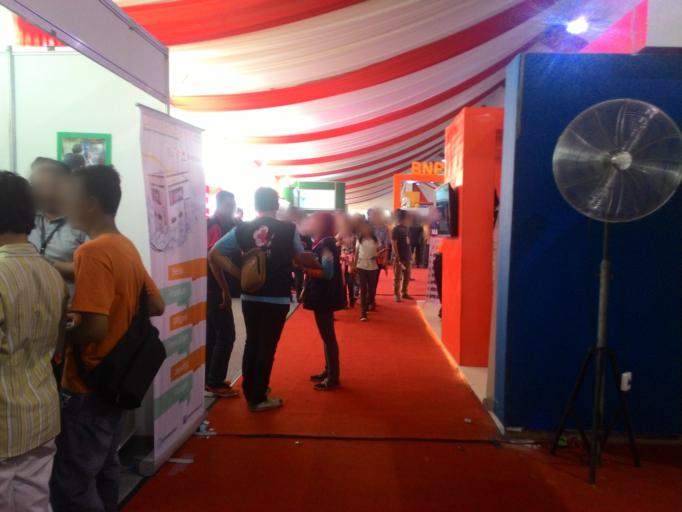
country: ID
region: Central Java
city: Surakarta
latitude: -7.5722
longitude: 110.8312
